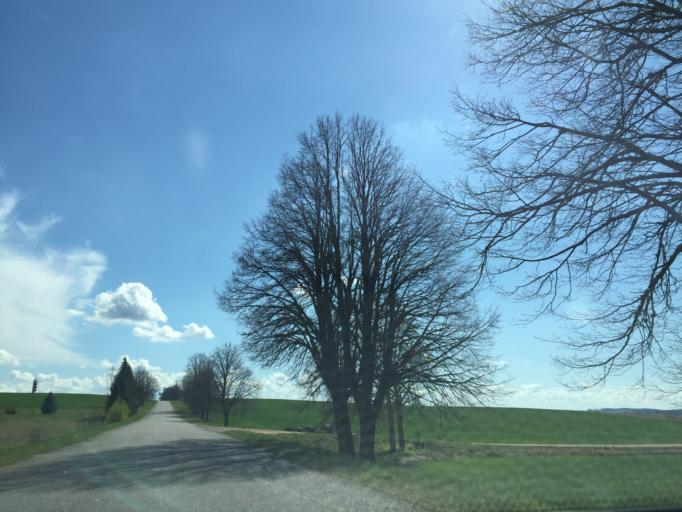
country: LV
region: Strenci
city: Strenci
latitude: 57.5545
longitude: 25.7122
